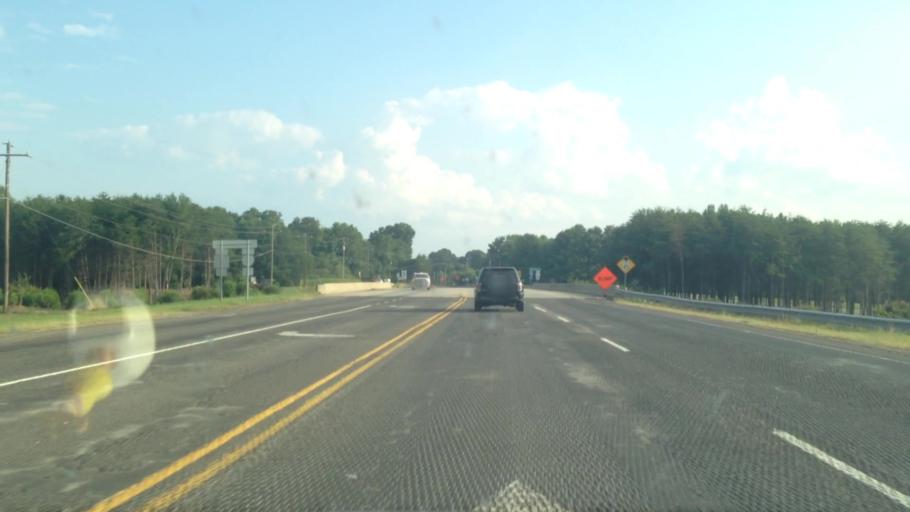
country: US
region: North Carolina
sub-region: Davidson County
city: Wallburg
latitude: 36.0276
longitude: -80.0581
